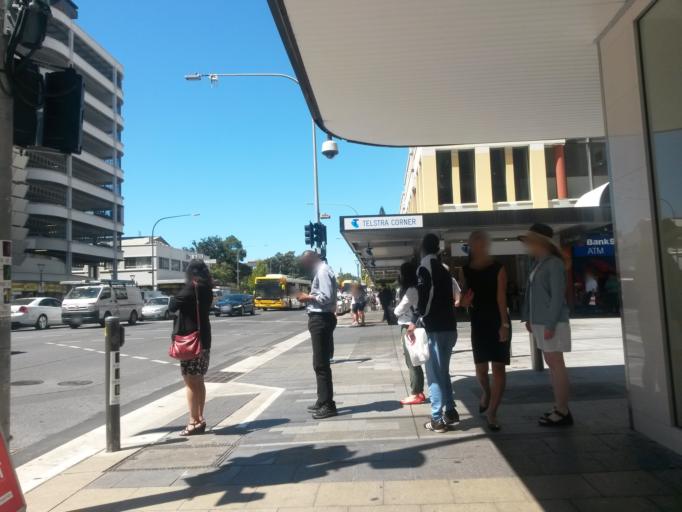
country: AU
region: South Australia
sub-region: Adelaide
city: Adelaide
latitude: -34.9224
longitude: 138.6057
